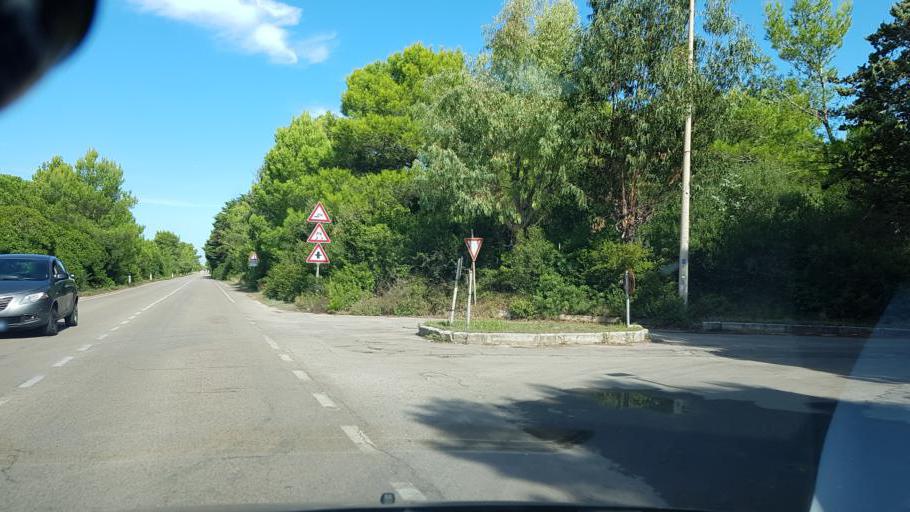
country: IT
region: Apulia
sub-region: Provincia di Lecce
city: Borgagne
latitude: 40.2452
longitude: 18.4421
